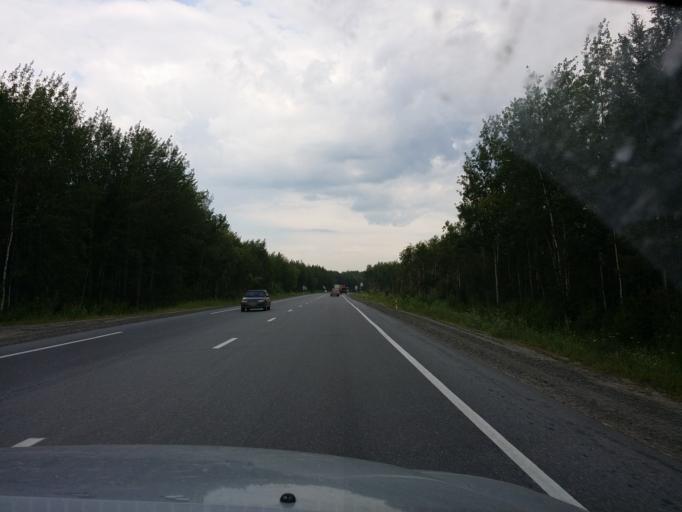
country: RU
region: Khanty-Mansiyskiy Avtonomnyy Okrug
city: Megion
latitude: 61.0524
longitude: 76.3212
